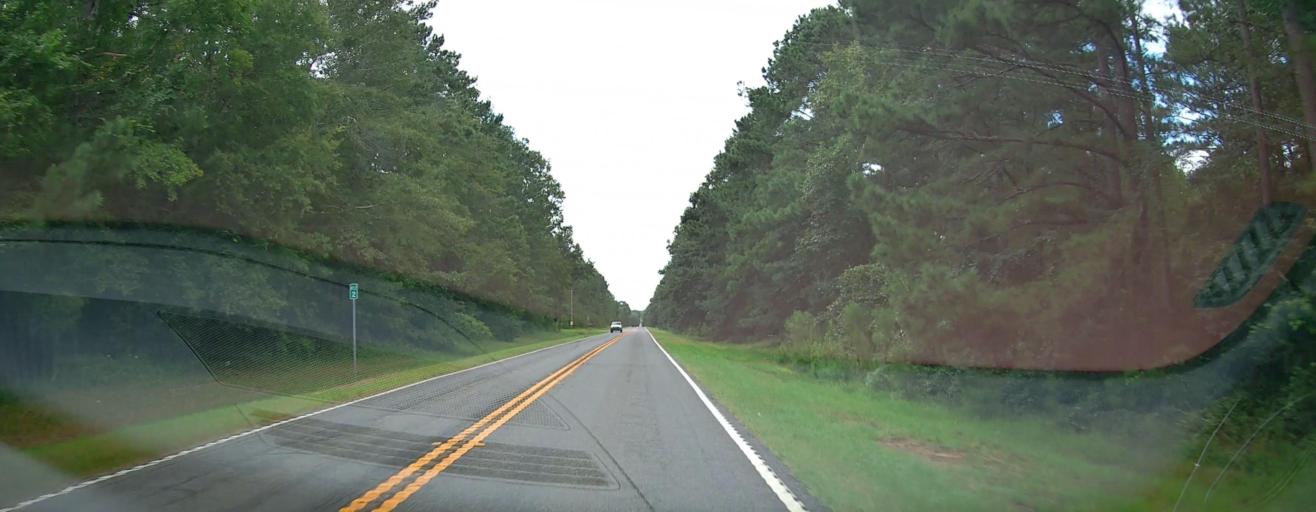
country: US
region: Georgia
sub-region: Dooly County
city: Unadilla
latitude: 32.2910
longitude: -83.8528
